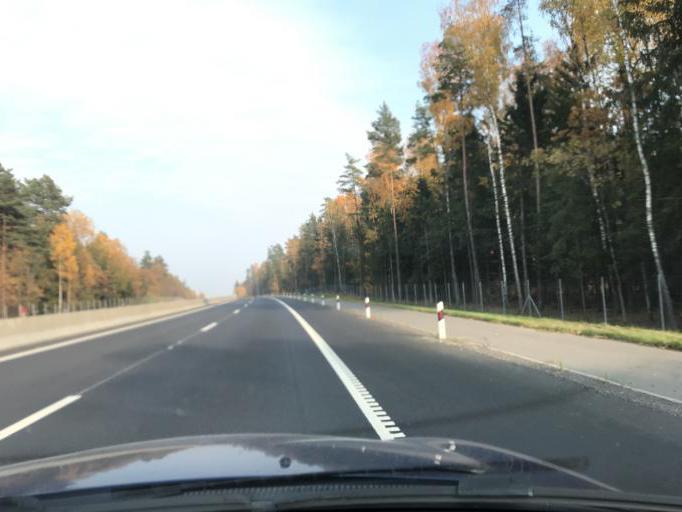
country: BY
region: Grodnenskaya
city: Shchuchin
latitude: 53.6687
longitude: 24.8269
